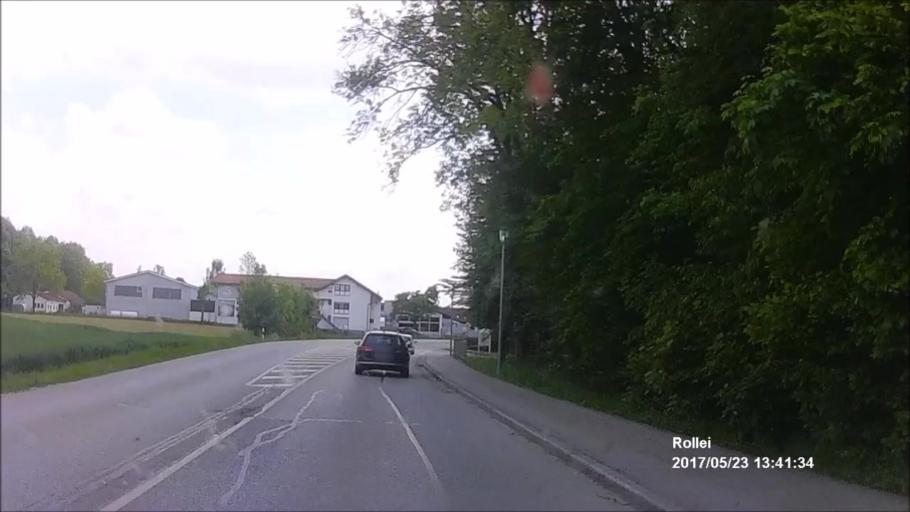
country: DE
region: Bavaria
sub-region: Upper Bavaria
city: Sankt Wolfgang
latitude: 48.2154
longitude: 12.1340
